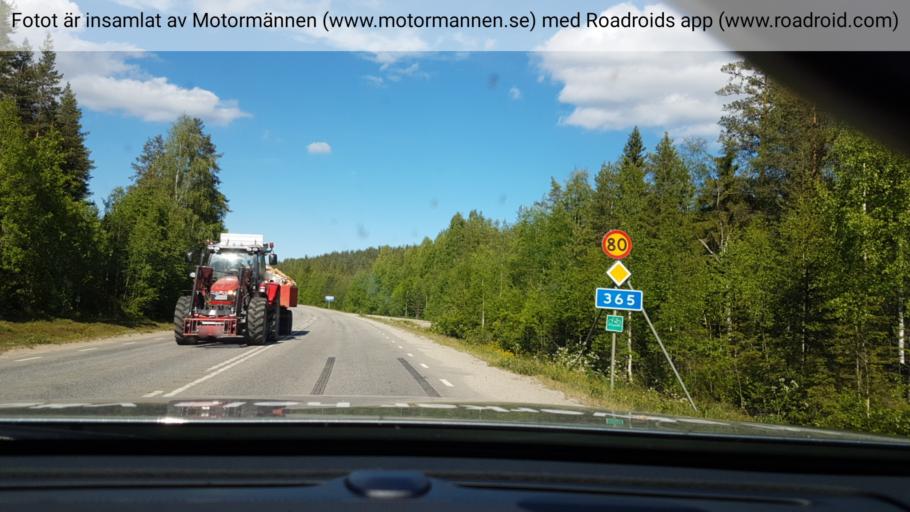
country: SE
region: Vaesterbotten
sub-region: Lycksele Kommun
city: Lycksele
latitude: 64.5764
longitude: 18.6537
